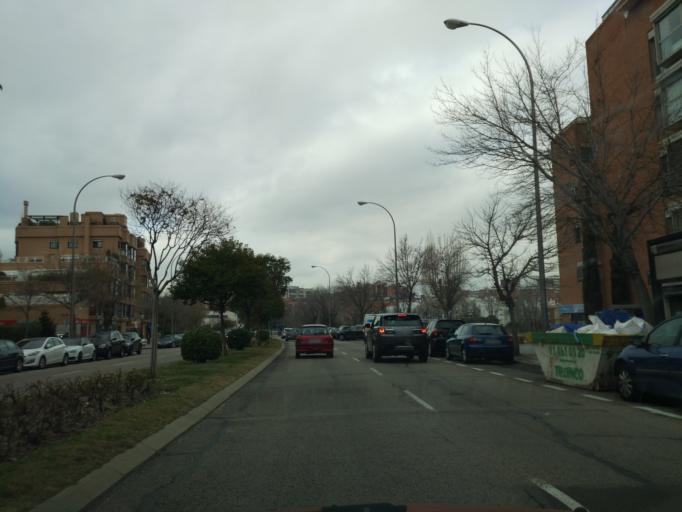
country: ES
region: Madrid
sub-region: Provincia de Madrid
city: Hortaleza
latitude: 40.4589
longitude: -3.6262
